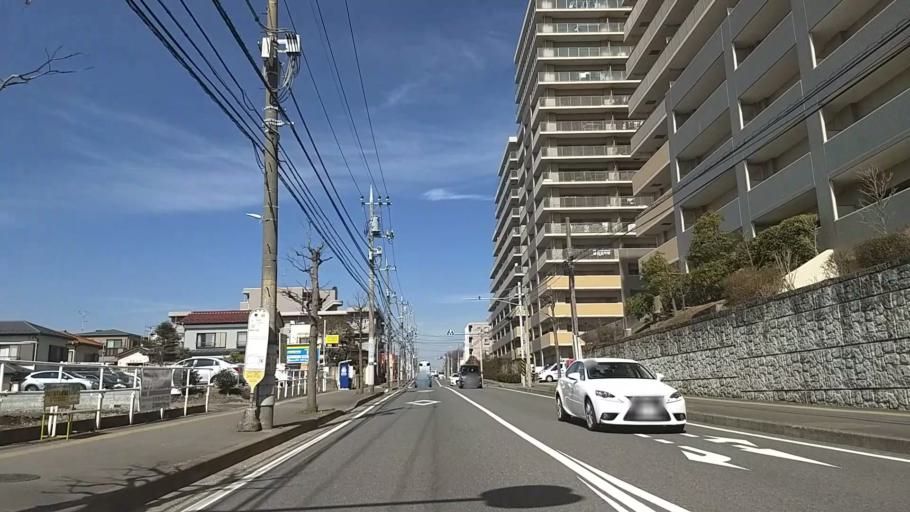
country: JP
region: Kanagawa
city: Fujisawa
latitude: 35.3978
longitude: 139.4626
